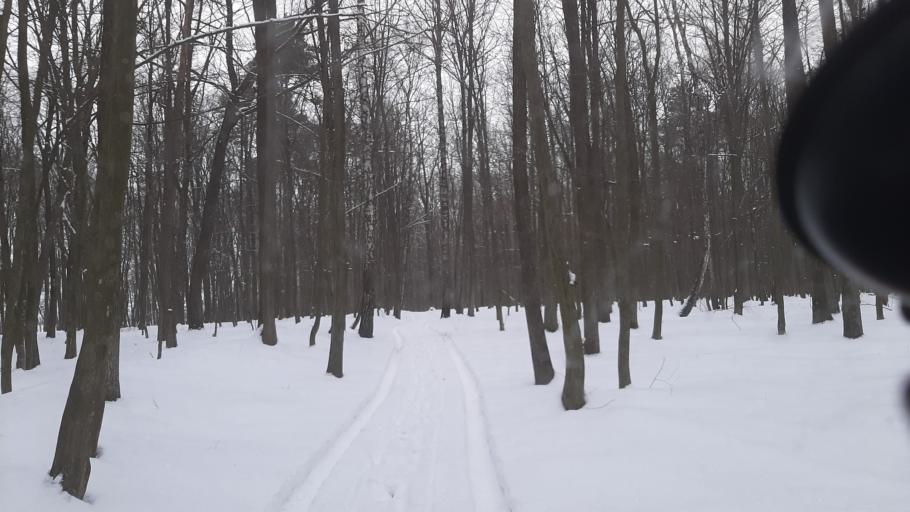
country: PL
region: Lublin Voivodeship
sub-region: Powiat lubelski
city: Garbow
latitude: 51.3720
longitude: 22.3898
